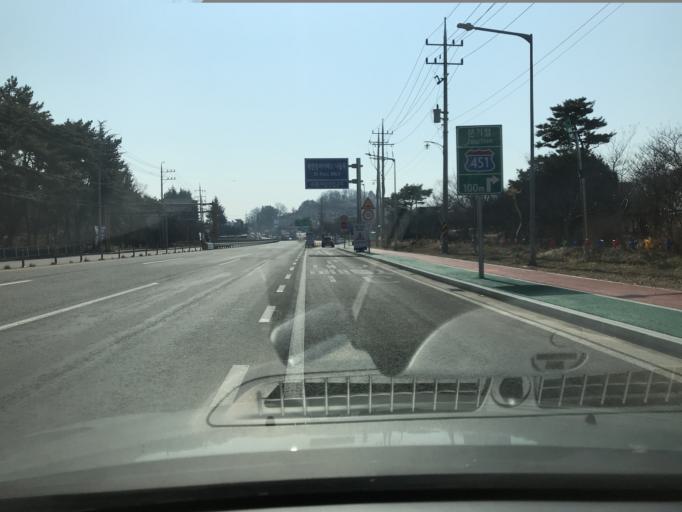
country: KR
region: Daegu
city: Hwawon
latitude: 35.7049
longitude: 128.4380
